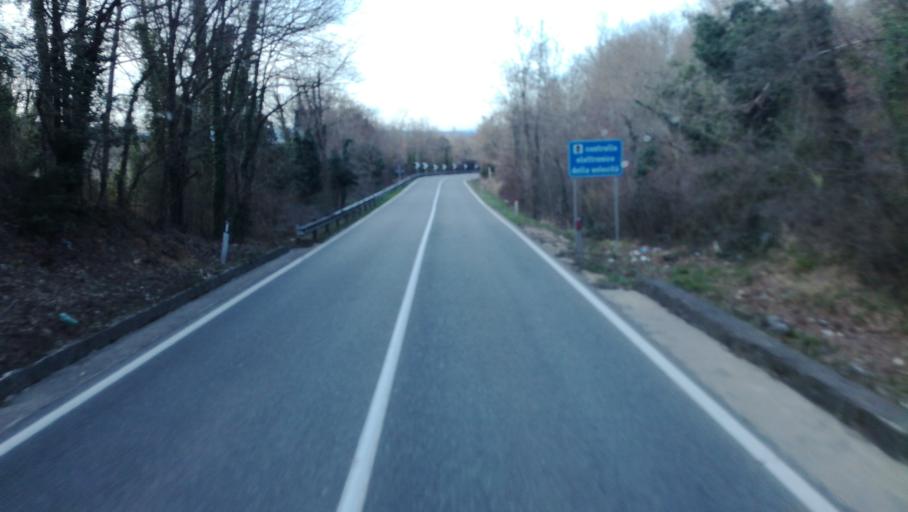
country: IT
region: Tuscany
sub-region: Provincia di Siena
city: Rosia
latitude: 43.1863
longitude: 11.2766
